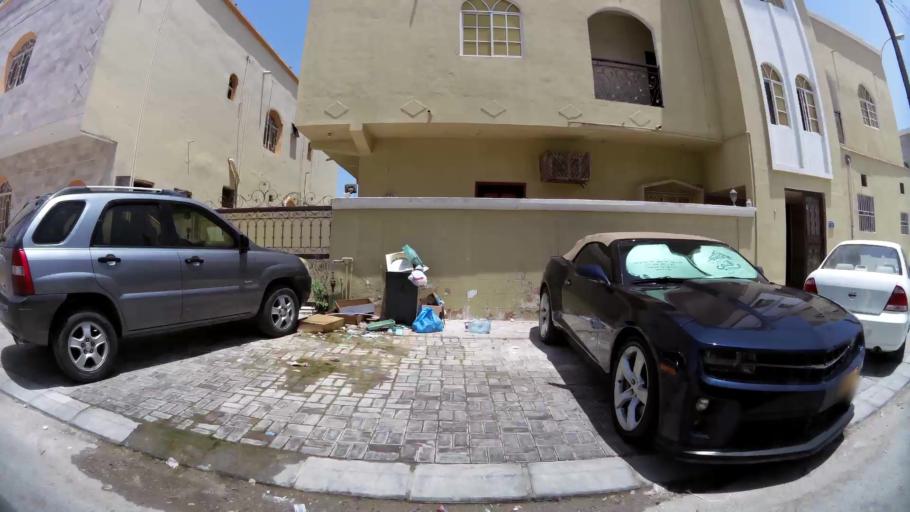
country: OM
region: Zufar
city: Salalah
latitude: 17.0195
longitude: 54.0830
